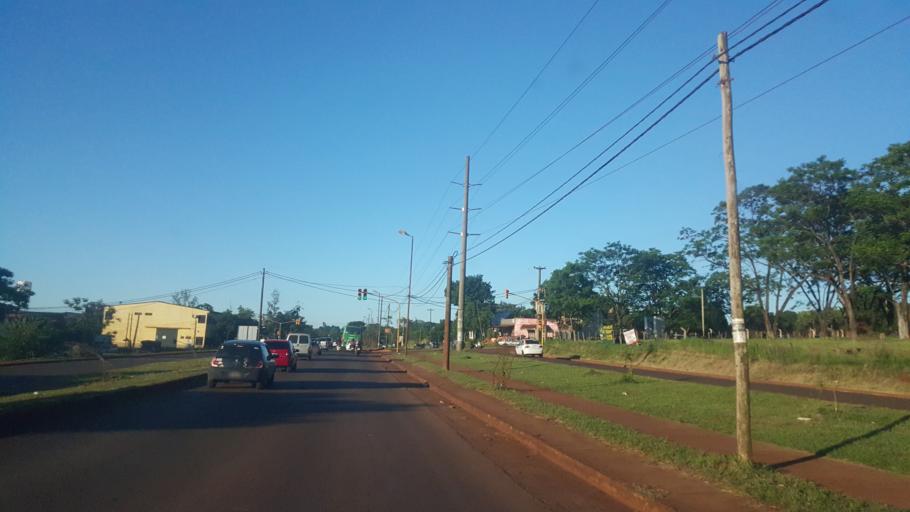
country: AR
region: Misiones
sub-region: Departamento de Capital
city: Posadas
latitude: -27.4227
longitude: -55.9326
